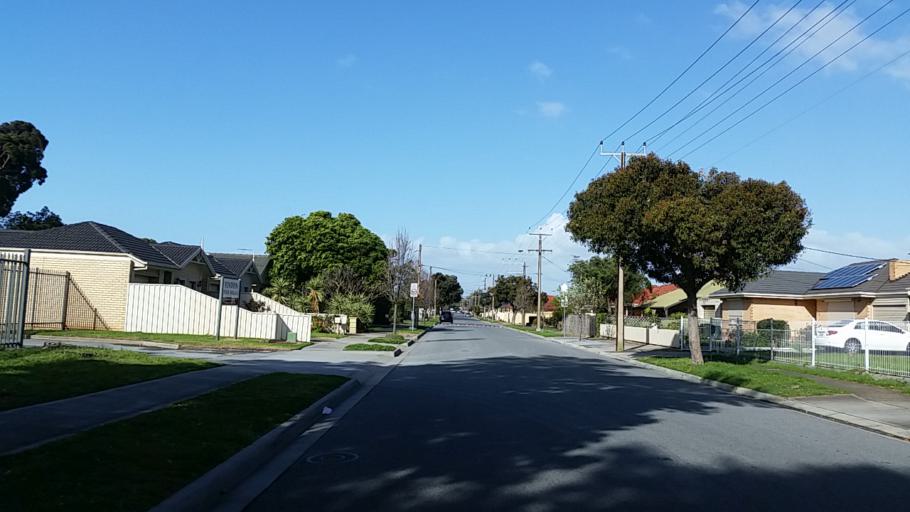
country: AU
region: South Australia
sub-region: Charles Sturt
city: Findon
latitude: -34.9004
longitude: 138.5257
